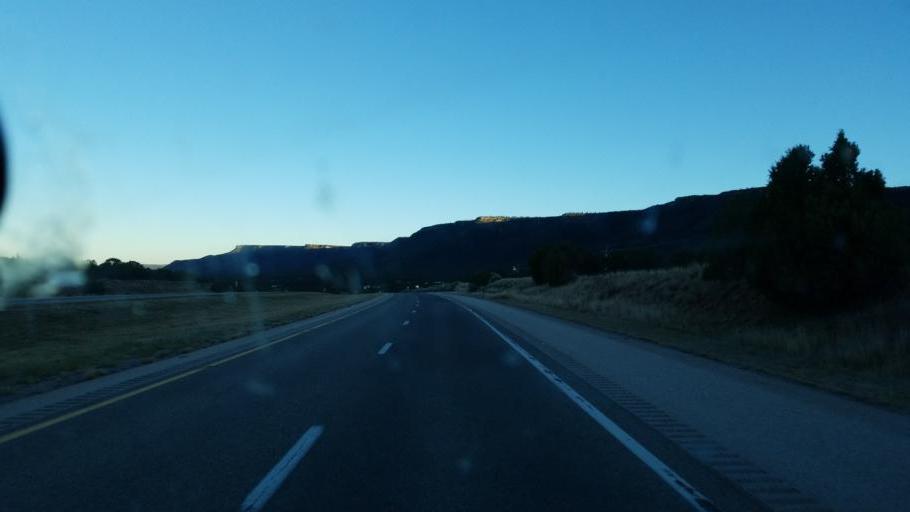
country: US
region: New Mexico
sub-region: San Miguel County
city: Pecos
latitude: 35.4325
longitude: -105.6022
